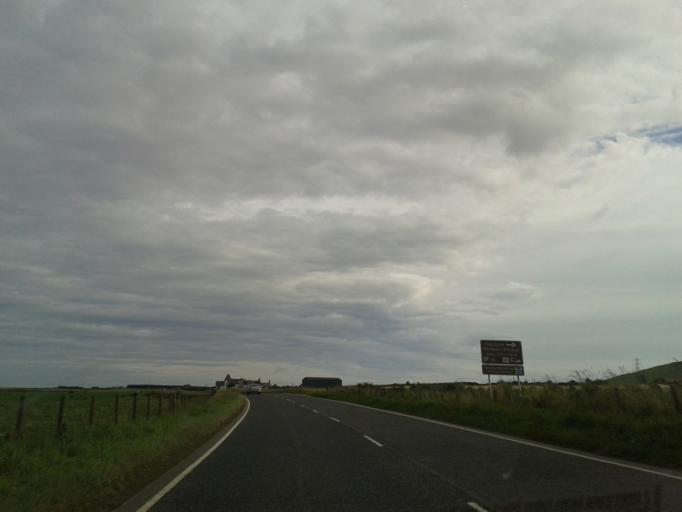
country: GB
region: Scotland
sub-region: Aberdeenshire
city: Portsoy
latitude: 57.6778
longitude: -2.7542
